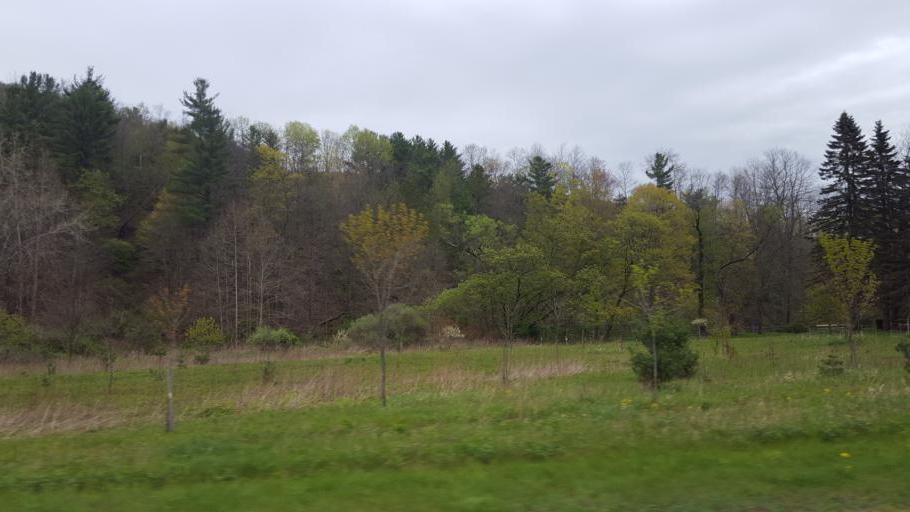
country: US
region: Pennsylvania
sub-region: Tioga County
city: Westfield
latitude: 41.9659
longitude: -77.4464
